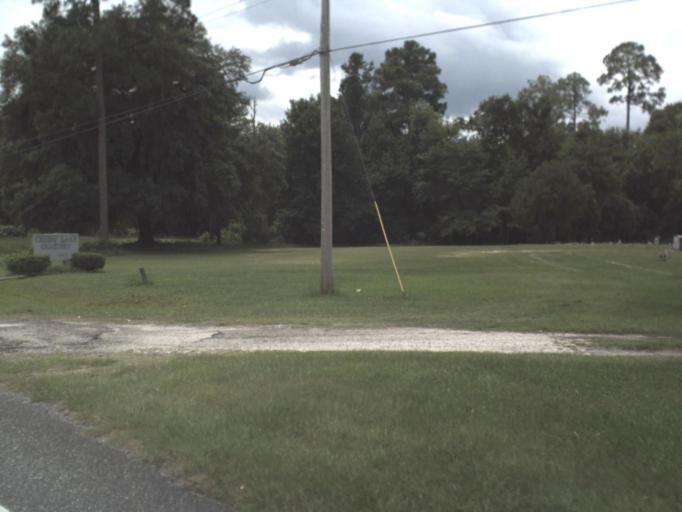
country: US
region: Florida
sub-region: Bradford County
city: Starke
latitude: 29.9510
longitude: -82.1457
